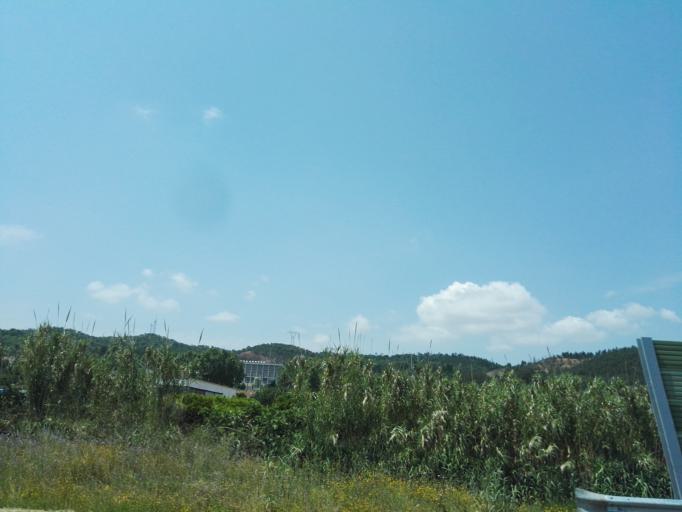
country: PT
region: Lisbon
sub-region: Vila Franca de Xira
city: Castanheira do Ribatejo
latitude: 38.9826
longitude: -8.9735
